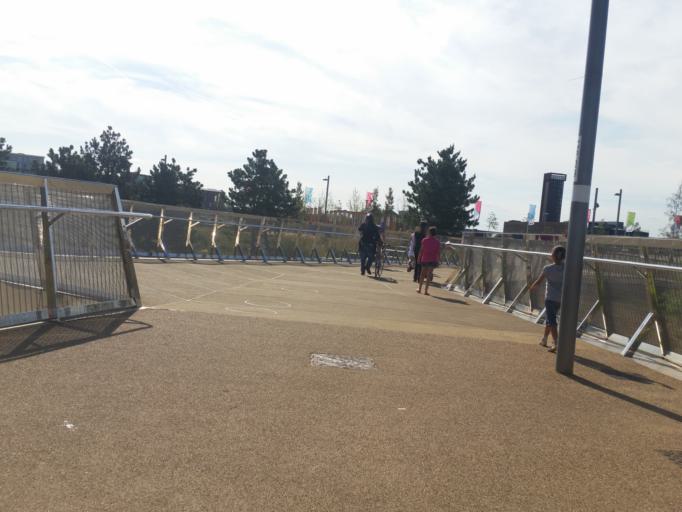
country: GB
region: England
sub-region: Greater London
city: Poplar
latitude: 51.5420
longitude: -0.0160
